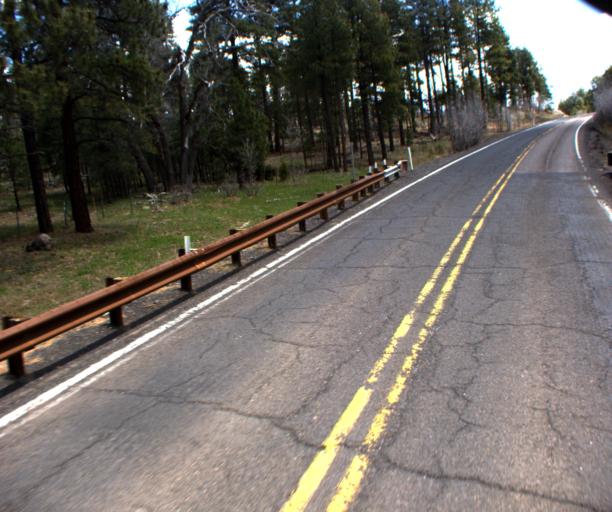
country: US
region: Arizona
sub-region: Coconino County
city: Kachina Village
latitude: 35.1089
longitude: -111.7212
